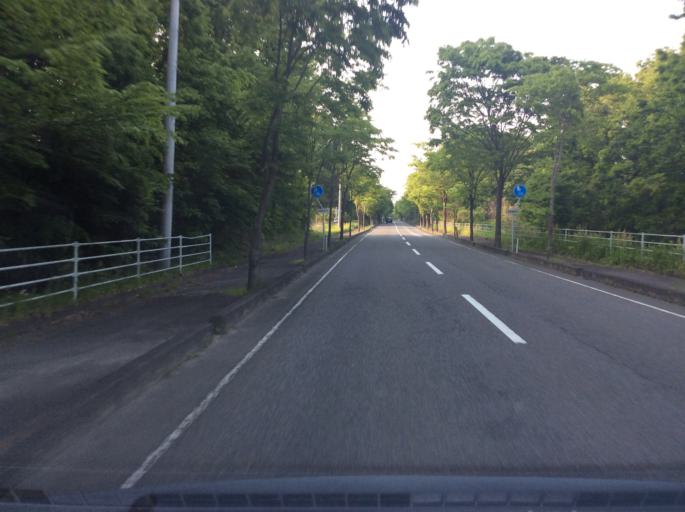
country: JP
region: Fukushima
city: Ishikawa
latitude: 37.2172
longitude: 140.4364
